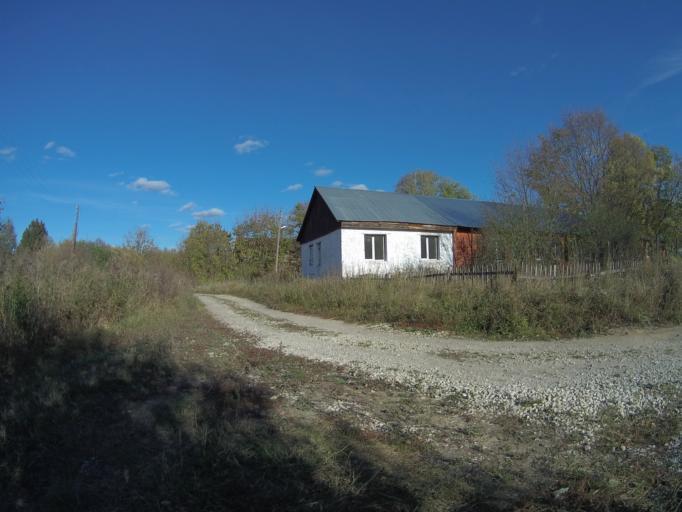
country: RU
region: Vladimir
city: Golovino
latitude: 55.9981
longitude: 40.5008
